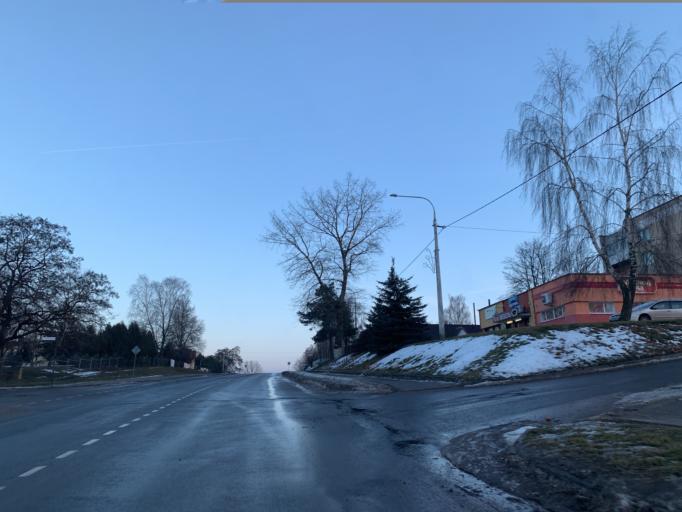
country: BY
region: Minsk
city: Nyasvizh
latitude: 53.2328
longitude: 26.6523
